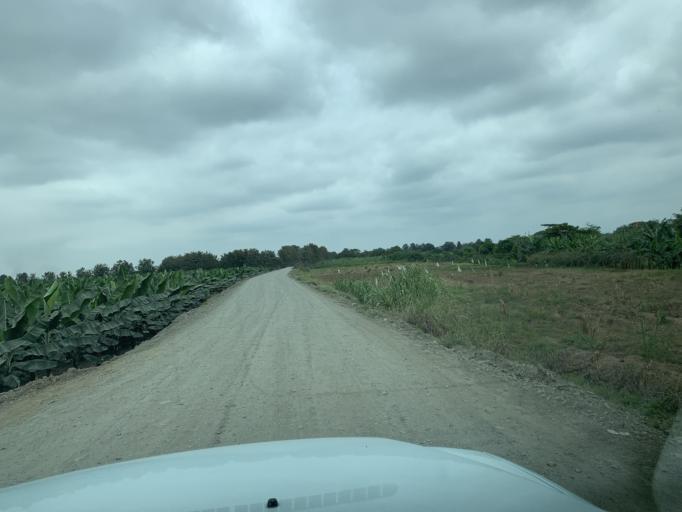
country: EC
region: Guayas
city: Coronel Marcelino Mariduena
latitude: -2.3286
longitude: -79.4568
